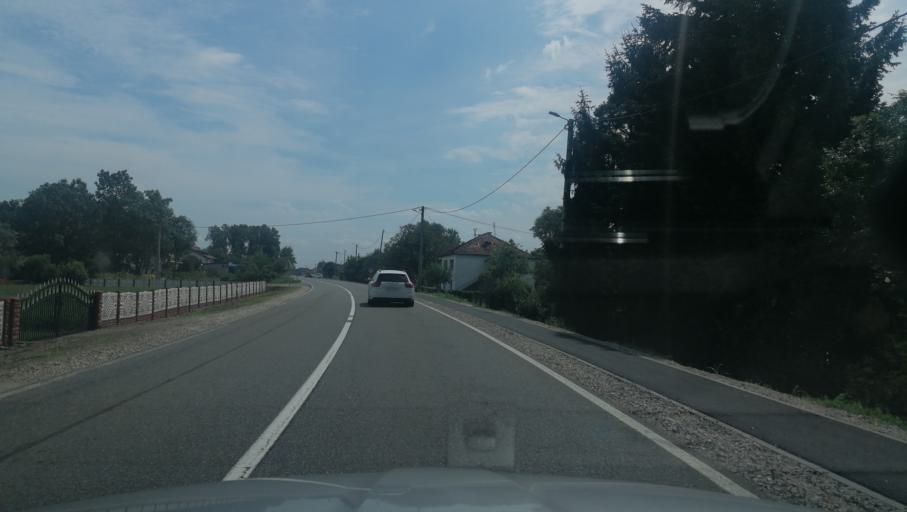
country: BA
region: Republika Srpska
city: Bosanski Samac
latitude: 45.0468
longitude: 18.4824
